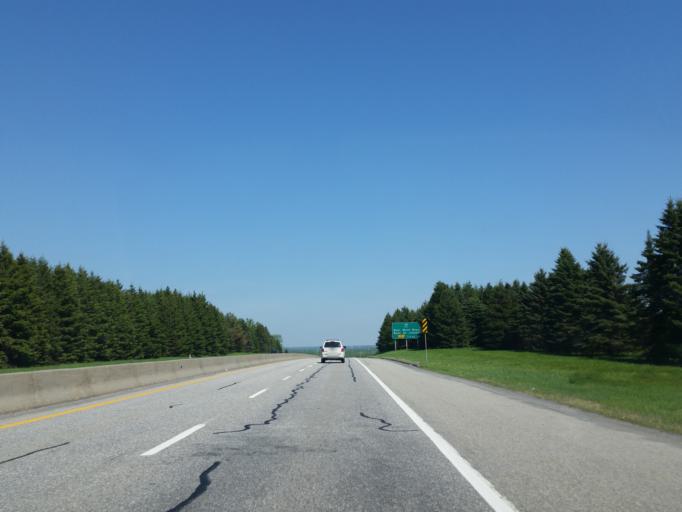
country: CA
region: Quebec
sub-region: Outaouais
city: Gatineau
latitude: 45.4711
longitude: -75.7614
